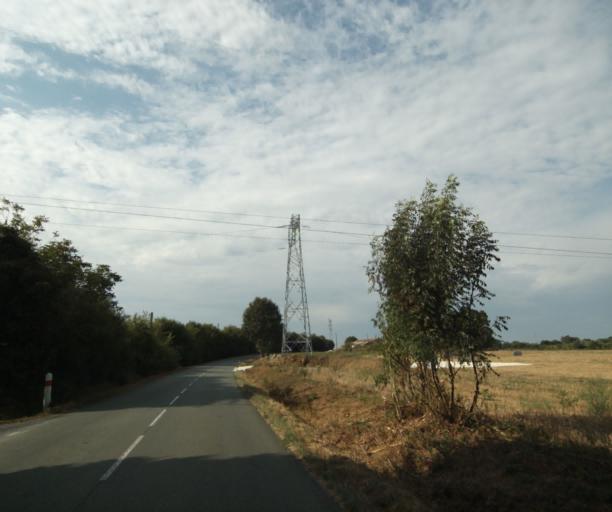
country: FR
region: Poitou-Charentes
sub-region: Departement de la Charente-Maritime
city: Cabariot
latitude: 45.9635
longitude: -0.8531
